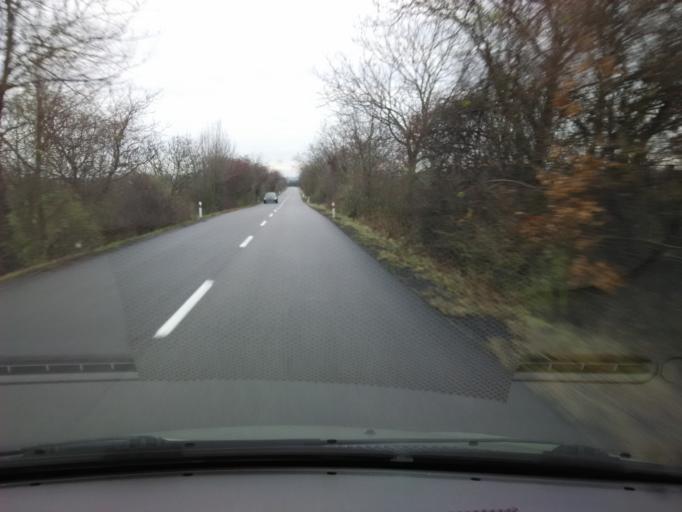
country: SK
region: Nitriansky
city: Tlmace
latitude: 48.3447
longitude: 18.4846
